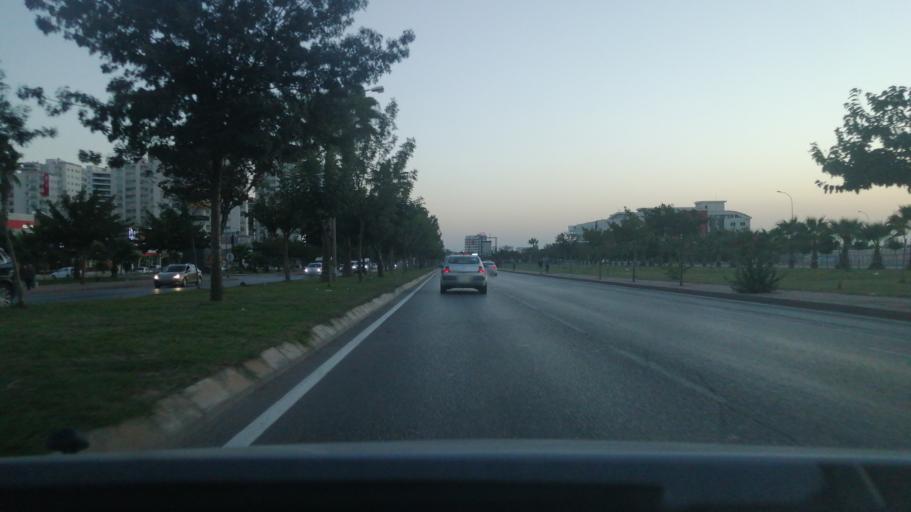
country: TR
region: Adana
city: Seyhan
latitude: 37.0214
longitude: 35.2530
